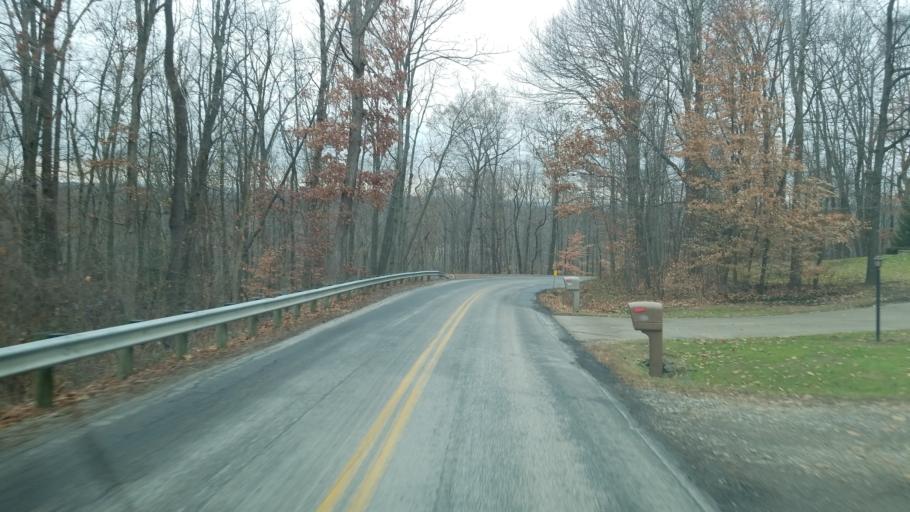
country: US
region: Ohio
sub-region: Holmes County
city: Millersburg
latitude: 40.5166
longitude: -81.8996
